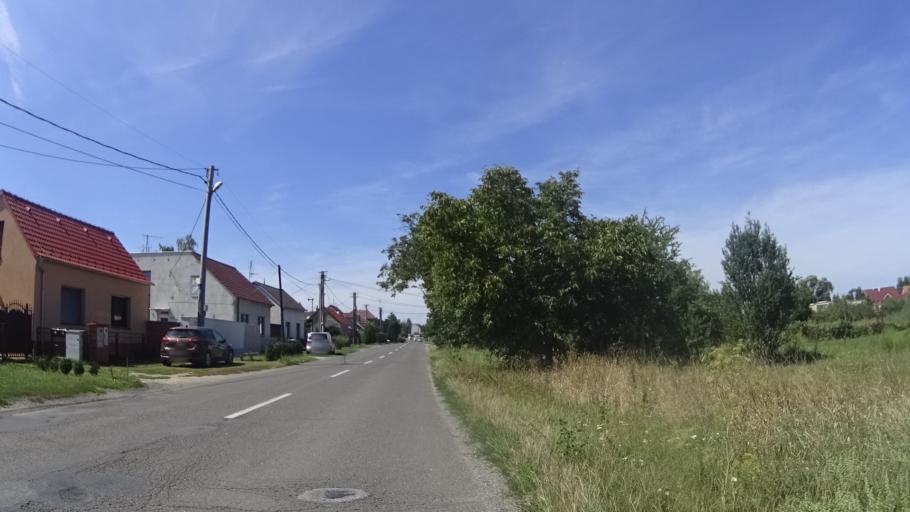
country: AT
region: Lower Austria
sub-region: Politischer Bezirk Ganserndorf
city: Marchegg
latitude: 48.3226
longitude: 16.9137
